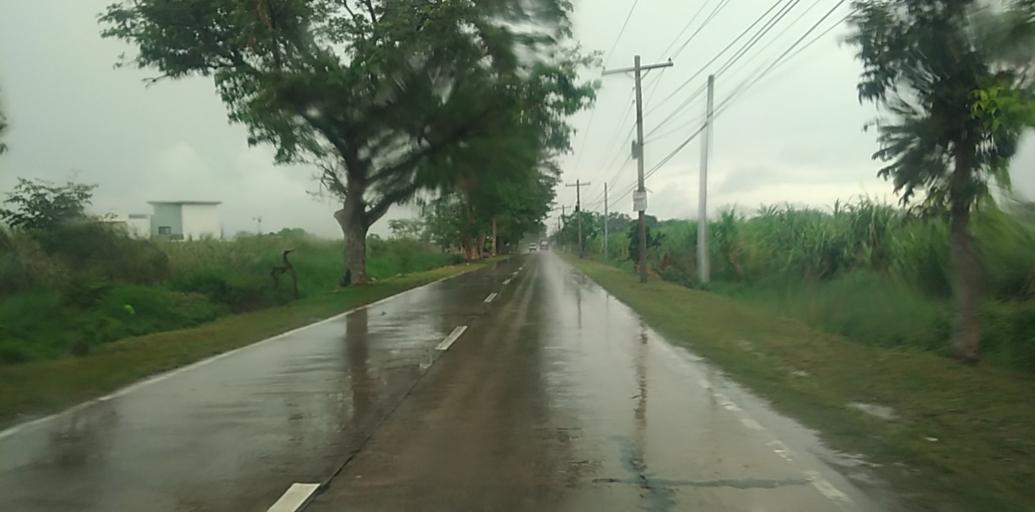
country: PH
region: Central Luzon
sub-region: Province of Pampanga
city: San Antonio
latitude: 15.1590
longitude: 120.6948
